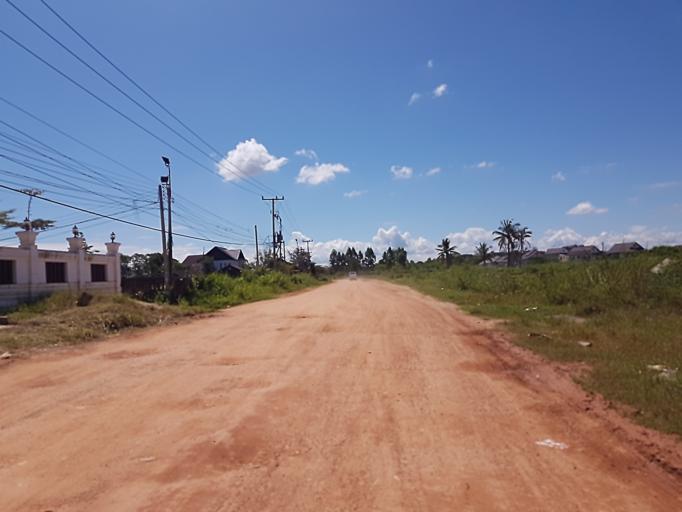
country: LA
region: Vientiane
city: Vientiane
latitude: 17.9272
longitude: 102.6323
